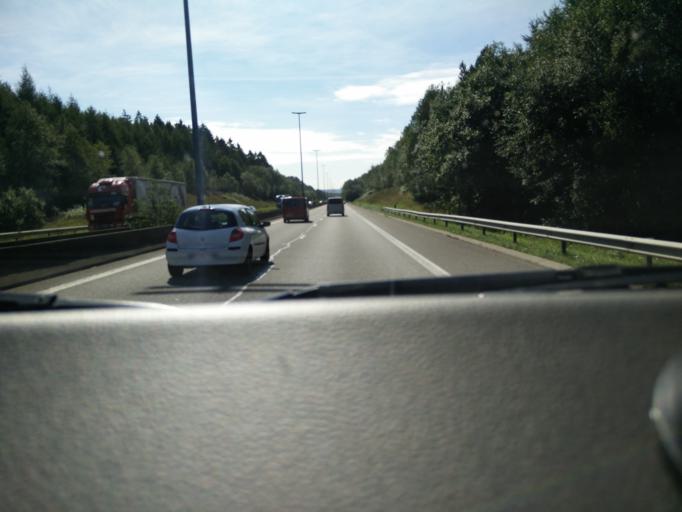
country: BE
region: Wallonia
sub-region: Province du Luxembourg
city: Libin
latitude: 49.9979
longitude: 5.2257
